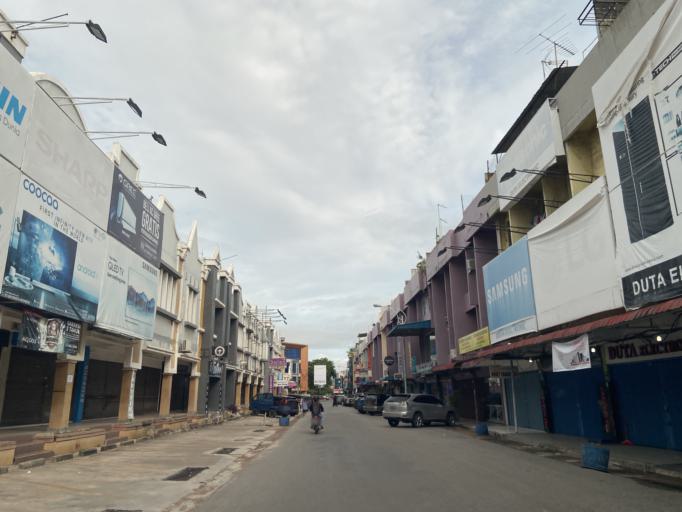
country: SG
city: Singapore
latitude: 1.1453
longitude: 104.0096
